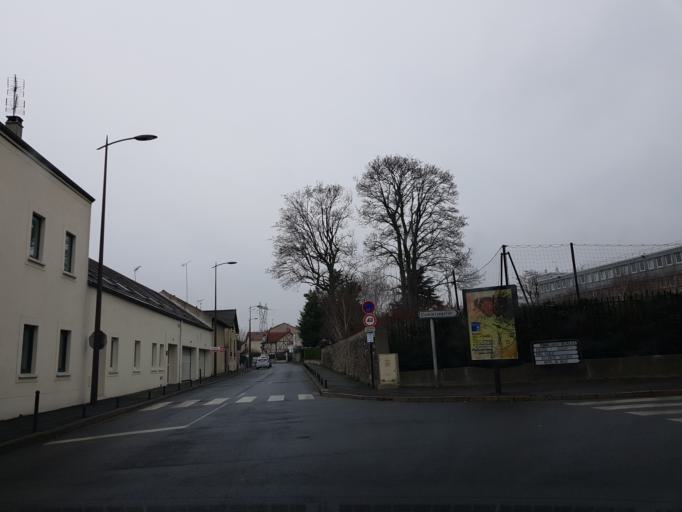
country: FR
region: Ile-de-France
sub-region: Departement du Val-de-Marne
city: Thiais
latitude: 48.7622
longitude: 2.3929
